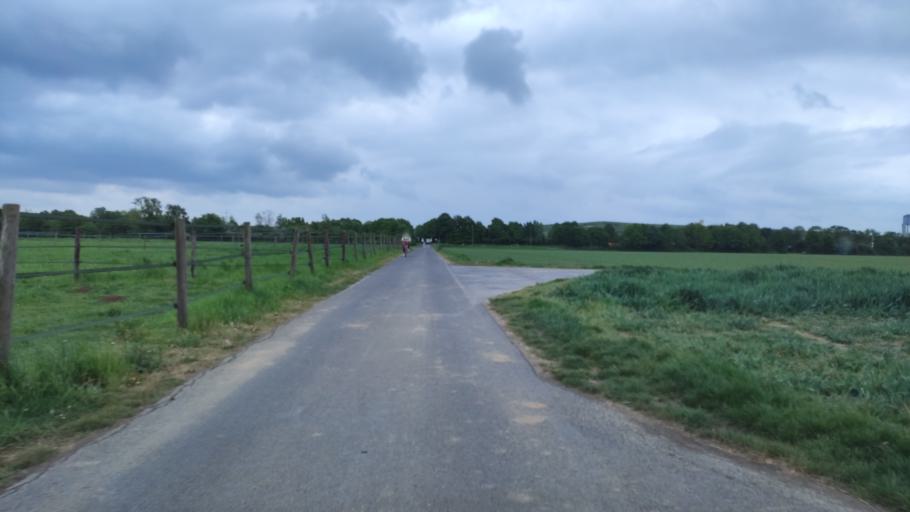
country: DE
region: North Rhine-Westphalia
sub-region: Regierungsbezirk Dusseldorf
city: Neuss
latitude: 51.1837
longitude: 6.6543
